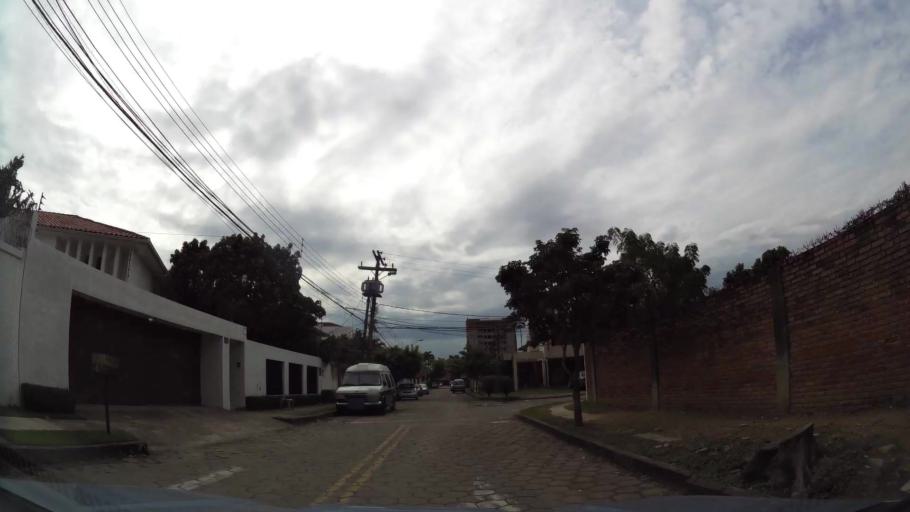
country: BO
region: Santa Cruz
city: Santa Cruz de la Sierra
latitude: -17.7972
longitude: -63.2001
